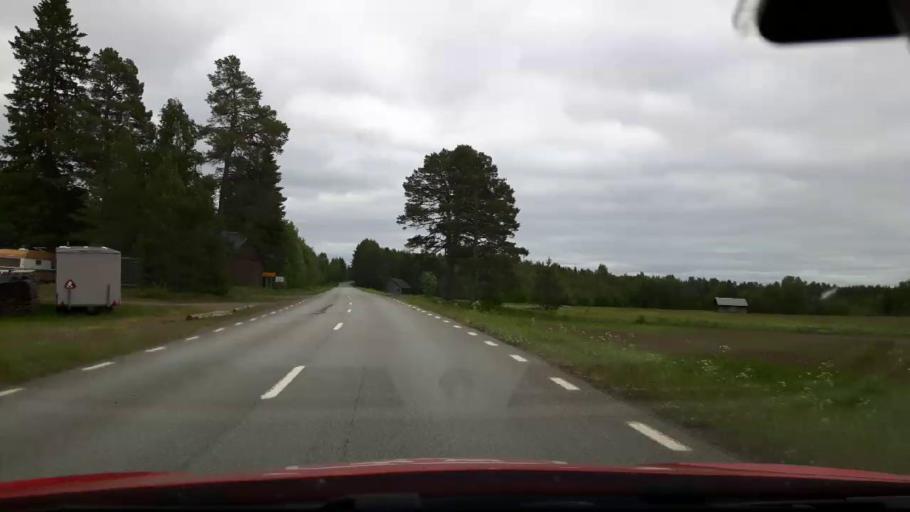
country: SE
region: Jaemtland
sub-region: Stroemsunds Kommun
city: Stroemsund
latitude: 63.5319
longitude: 15.4500
